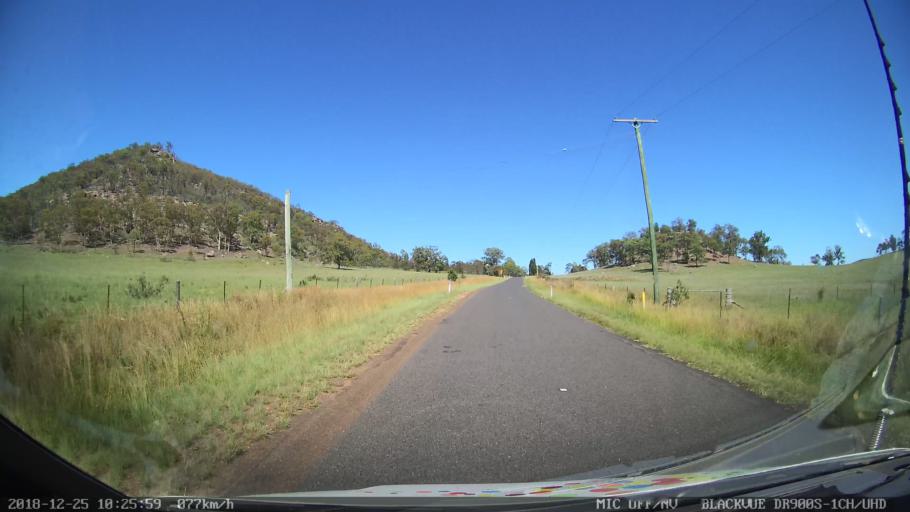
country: AU
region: New South Wales
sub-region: Muswellbrook
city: Denman
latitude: -32.3912
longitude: 150.4909
